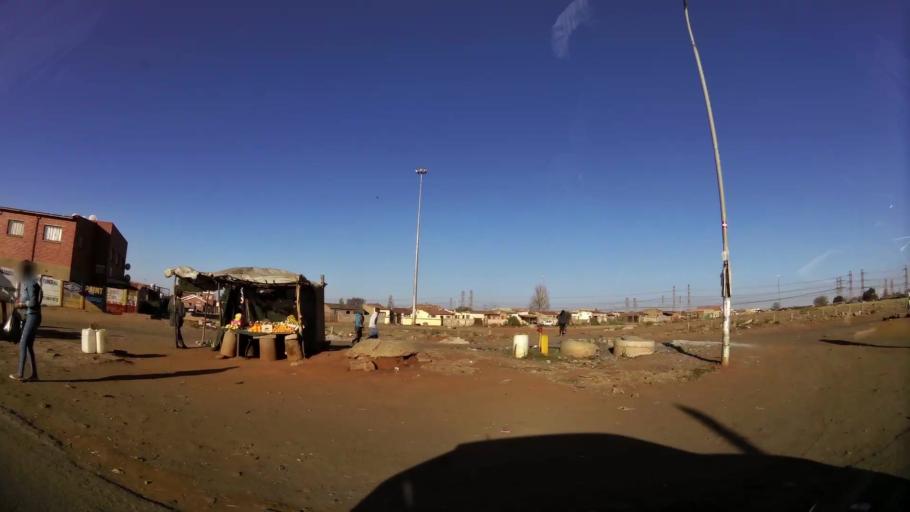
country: ZA
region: Gauteng
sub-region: Ekurhuleni Metropolitan Municipality
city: Tembisa
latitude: -26.0137
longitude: 28.2416
